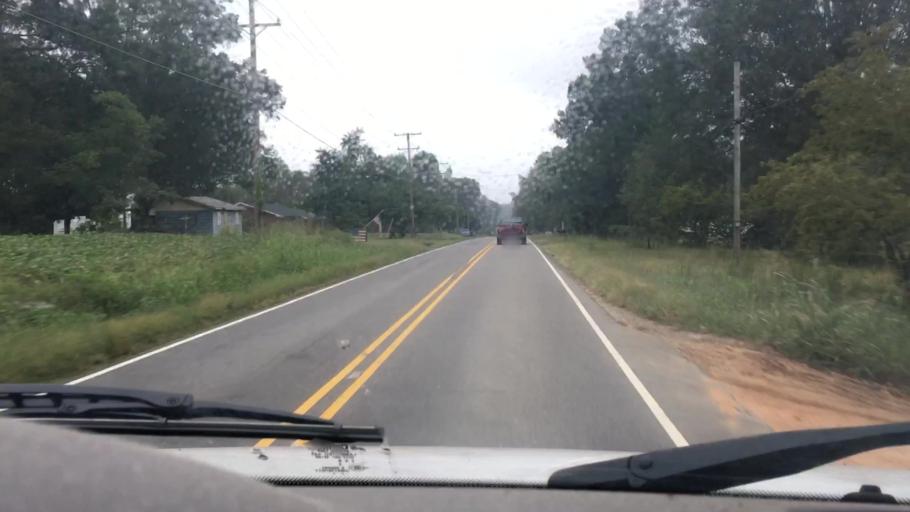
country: US
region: North Carolina
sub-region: Iredell County
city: Mooresville
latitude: 35.6291
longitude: -80.7795
